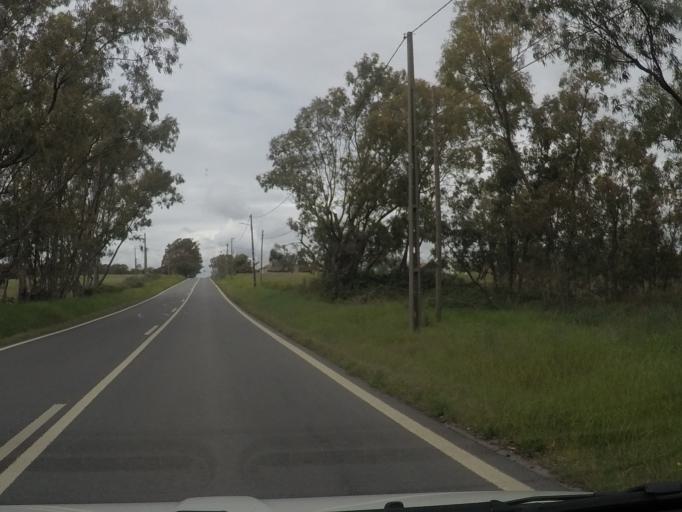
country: PT
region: Setubal
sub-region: Santiago do Cacem
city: Cercal
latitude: 37.8617
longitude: -8.7173
